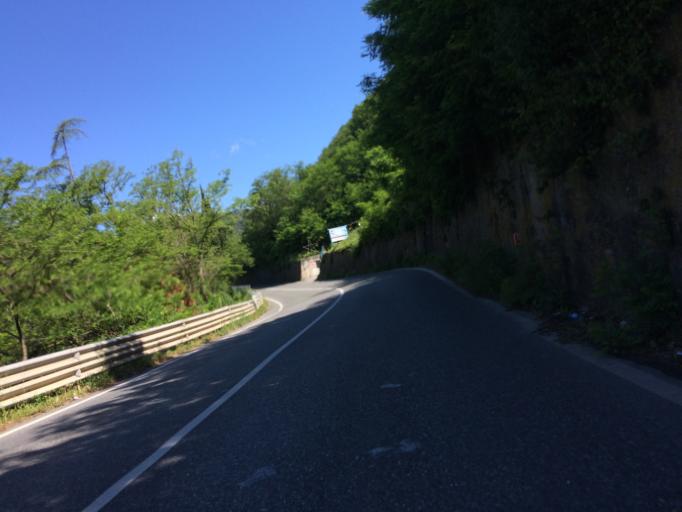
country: IT
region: Tuscany
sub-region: Provincia di Massa-Carrara
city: Albiano Magra
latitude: 44.1791
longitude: 9.9283
